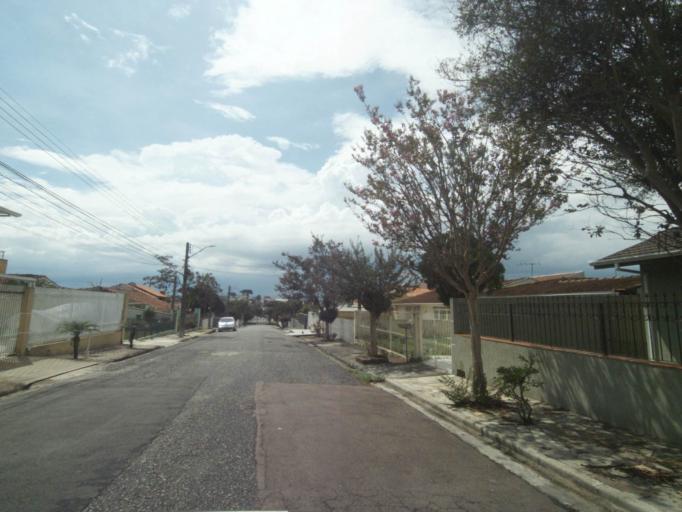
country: BR
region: Parana
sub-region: Pinhais
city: Pinhais
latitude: -25.4737
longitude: -49.2082
